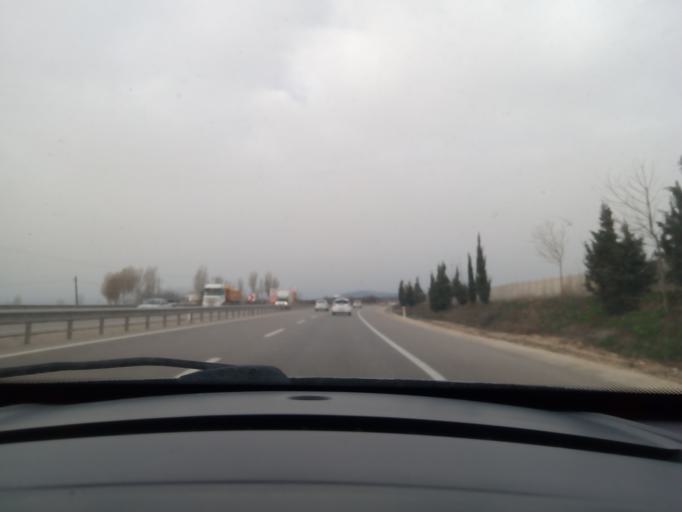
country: TR
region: Bursa
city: Mahmudiye
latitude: 40.2087
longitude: 28.5947
